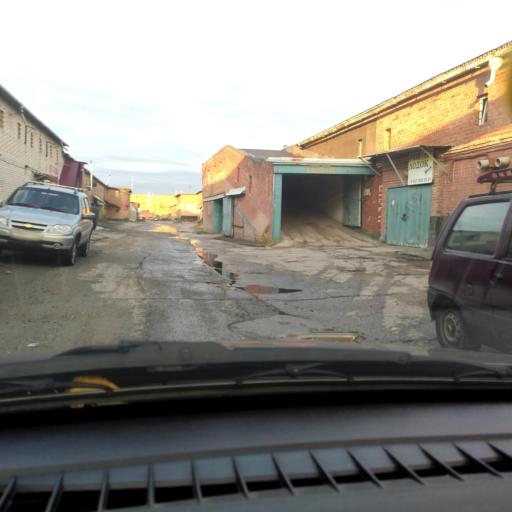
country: RU
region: Samara
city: Tol'yatti
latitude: 53.5390
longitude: 49.2935
